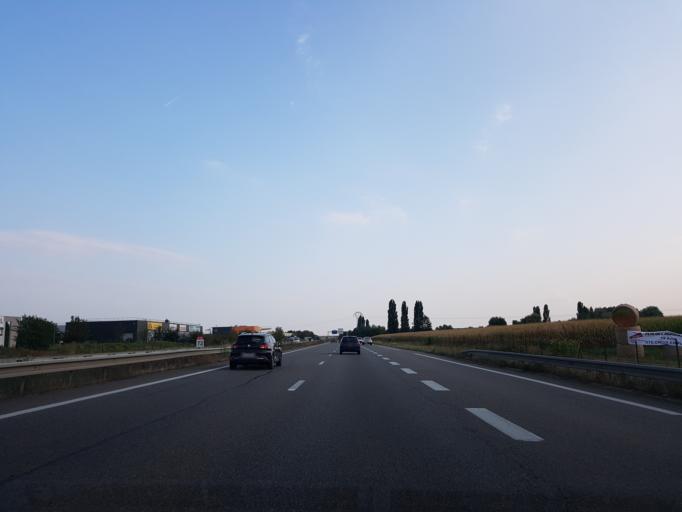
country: FR
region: Alsace
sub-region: Departement du Haut-Rhin
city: Sainte-Croix-en-Plaine
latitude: 48.0219
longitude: 7.3730
